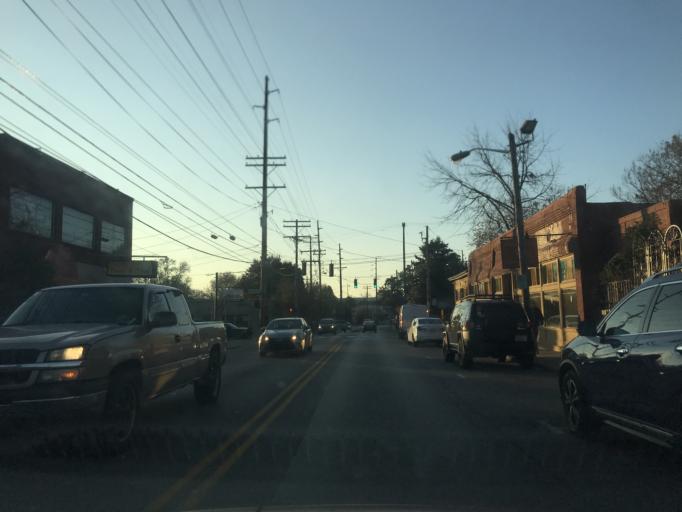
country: US
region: Indiana
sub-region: Clark County
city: Jeffersonville
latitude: 38.2535
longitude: -85.7055
